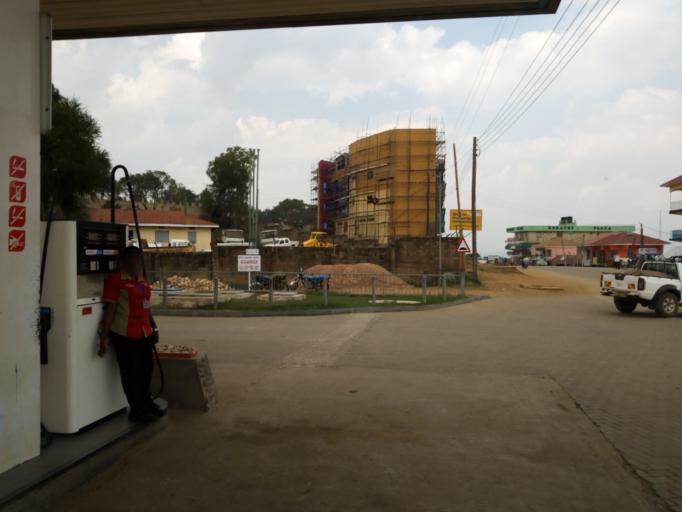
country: UG
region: Western Region
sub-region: Rukungiri District
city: Rukungiri
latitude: -0.7871
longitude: 29.9264
